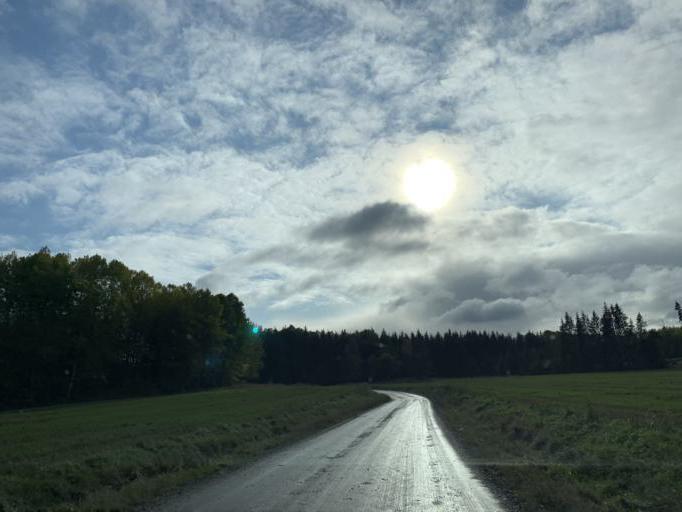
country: SE
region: Soedermanland
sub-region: Eskilstuna Kommun
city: Kvicksund
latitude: 59.3971
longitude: 16.2371
